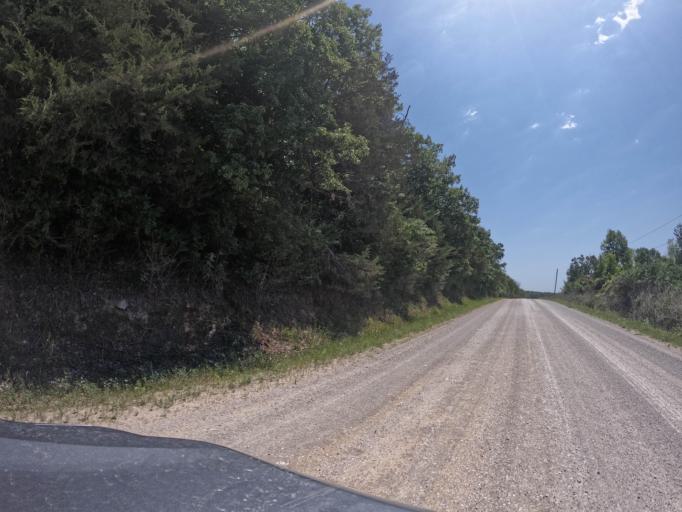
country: US
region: Iowa
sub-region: Henry County
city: Mount Pleasant
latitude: 40.8936
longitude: -91.5460
